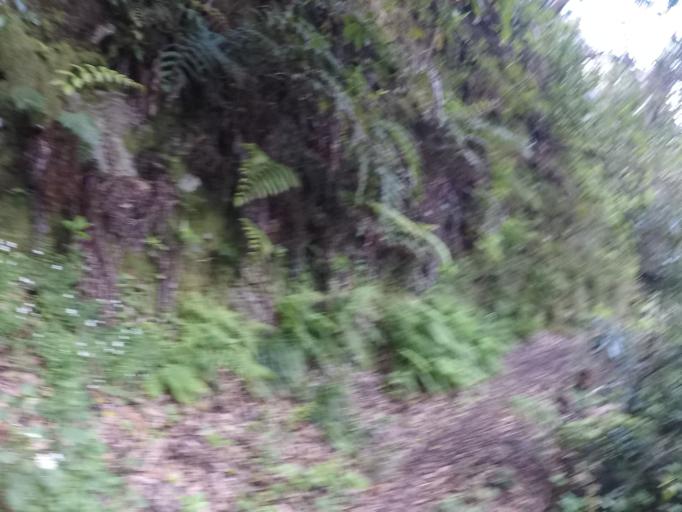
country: PT
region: Madeira
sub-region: Camara de Lobos
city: Curral das Freiras
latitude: 32.7469
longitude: -17.0009
